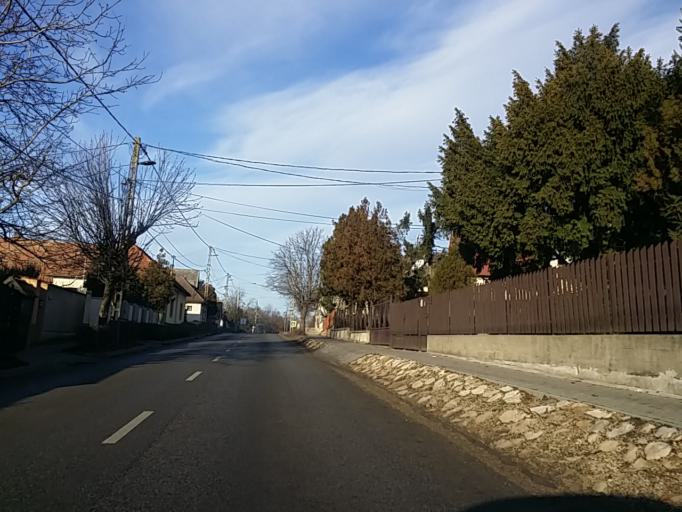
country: HU
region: Pest
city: Telki
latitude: 47.5456
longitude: 18.8309
